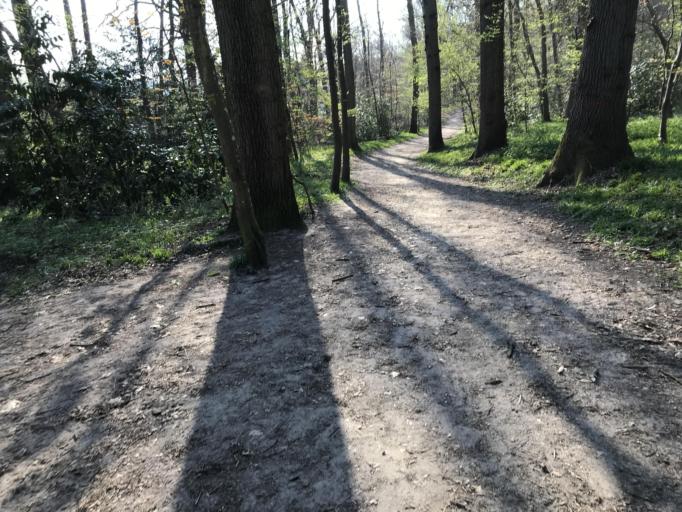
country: FR
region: Ile-de-France
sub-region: Departement de l'Essonne
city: Bures-sur-Yvette
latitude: 48.7053
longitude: 2.1661
